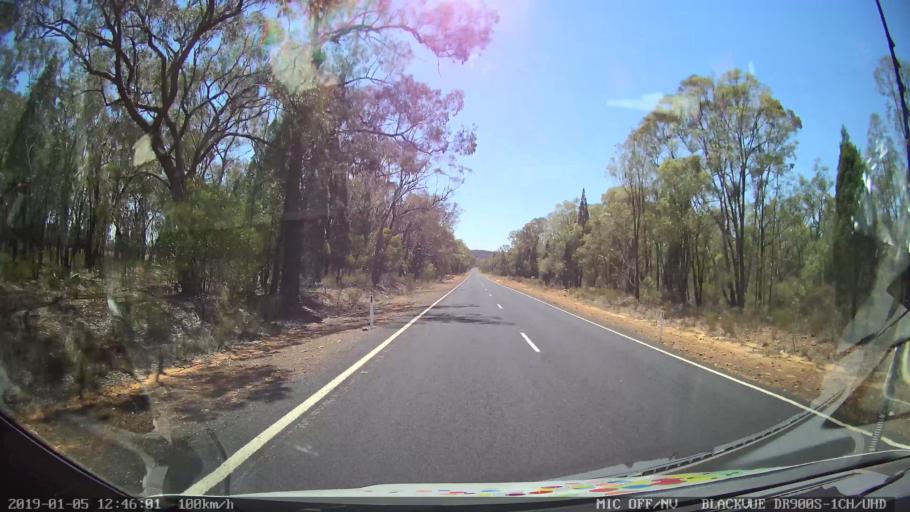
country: AU
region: New South Wales
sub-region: Warrumbungle Shire
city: Coonabarabran
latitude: -31.1223
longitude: 149.5571
